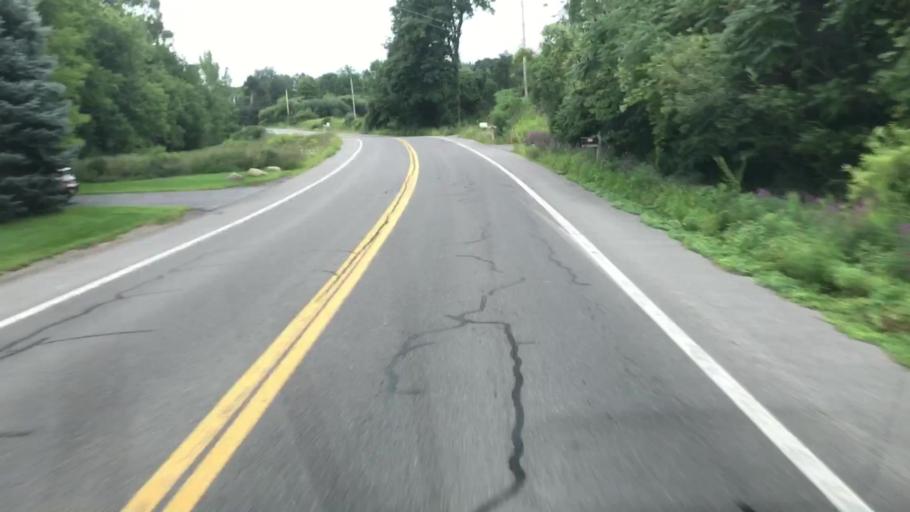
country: US
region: New York
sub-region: Onondaga County
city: Camillus
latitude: 43.0546
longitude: -76.3146
